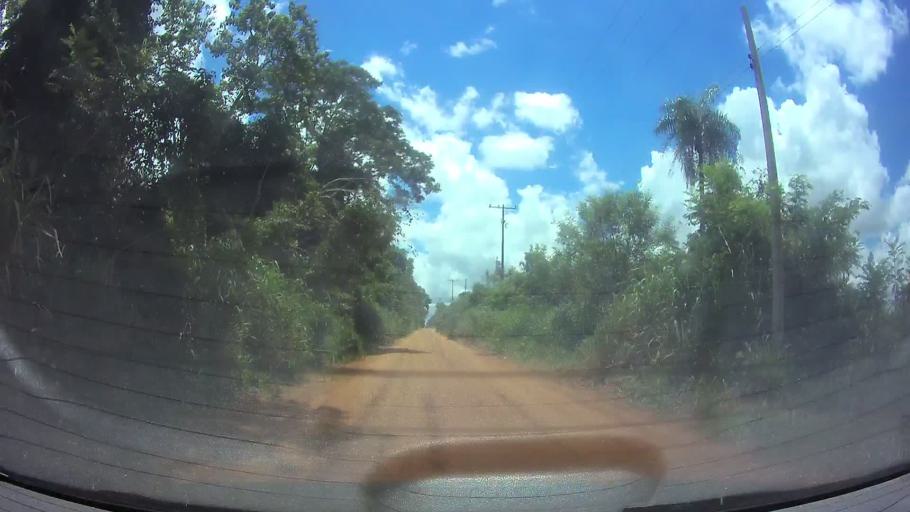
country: PY
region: Paraguari
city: La Colmena
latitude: -25.9134
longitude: -56.7950
